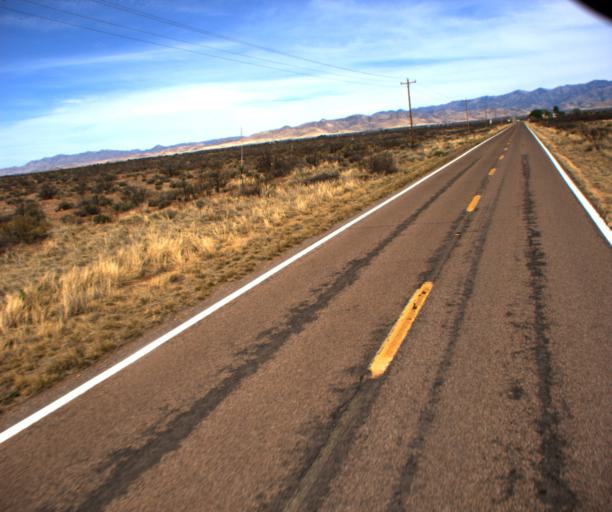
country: US
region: Arizona
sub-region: Cochise County
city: Willcox
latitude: 31.8761
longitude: -109.5826
